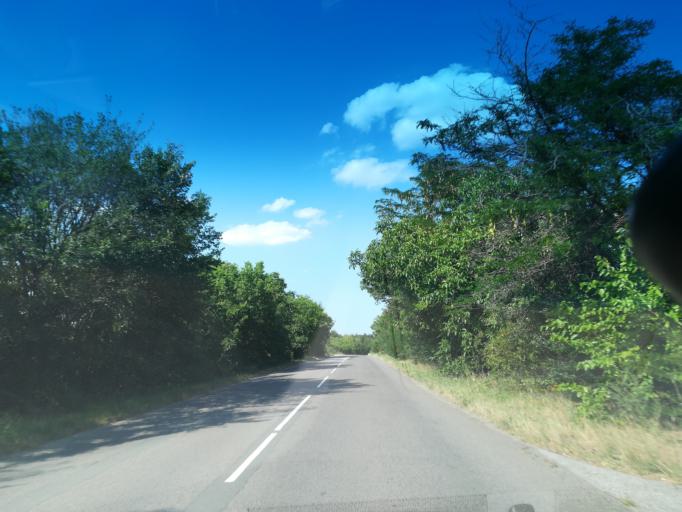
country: BG
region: Stara Zagora
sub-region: Obshtina Chirpan
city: Chirpan
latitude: 42.2266
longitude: 25.3912
